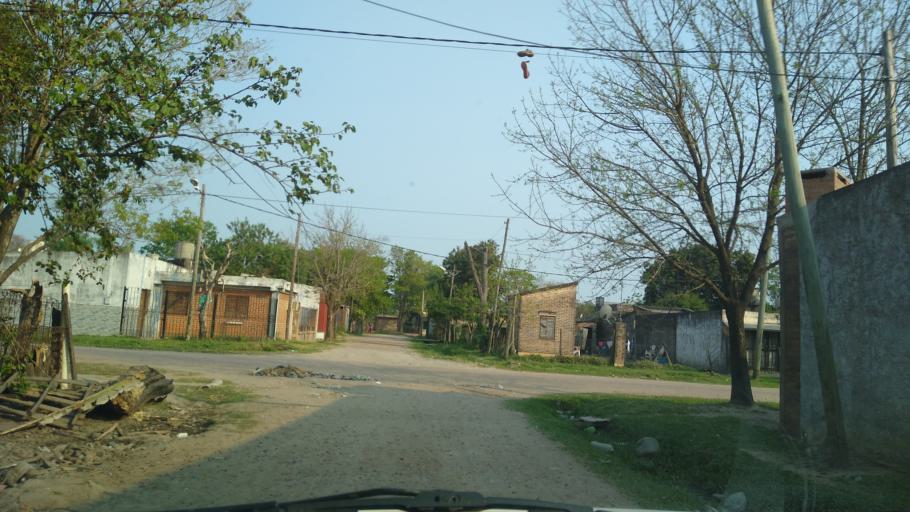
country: AR
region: Chaco
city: Resistencia
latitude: -27.4857
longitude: -58.9724
